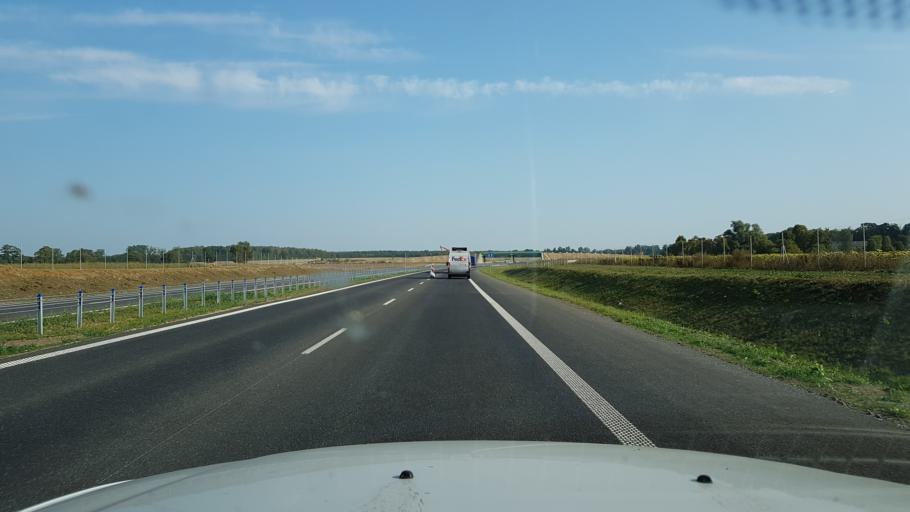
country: PL
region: West Pomeranian Voivodeship
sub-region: Powiat gryficki
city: Ploty
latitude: 53.7700
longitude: 15.2366
